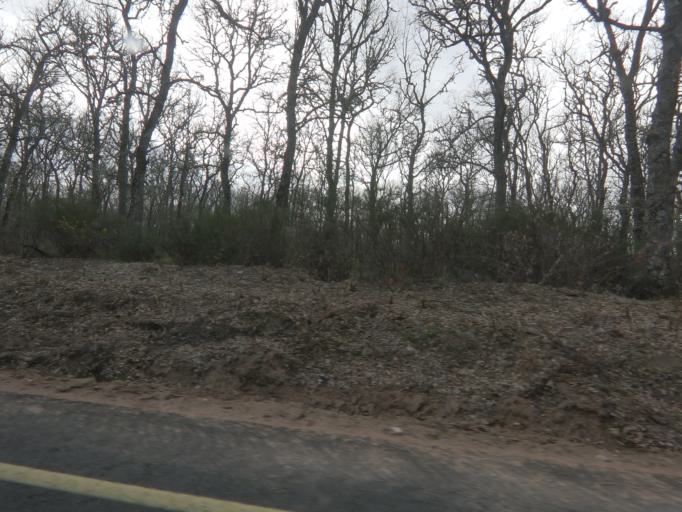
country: ES
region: Castille and Leon
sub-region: Provincia de Salamanca
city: Villasrubias
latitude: 40.3317
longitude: -6.6450
